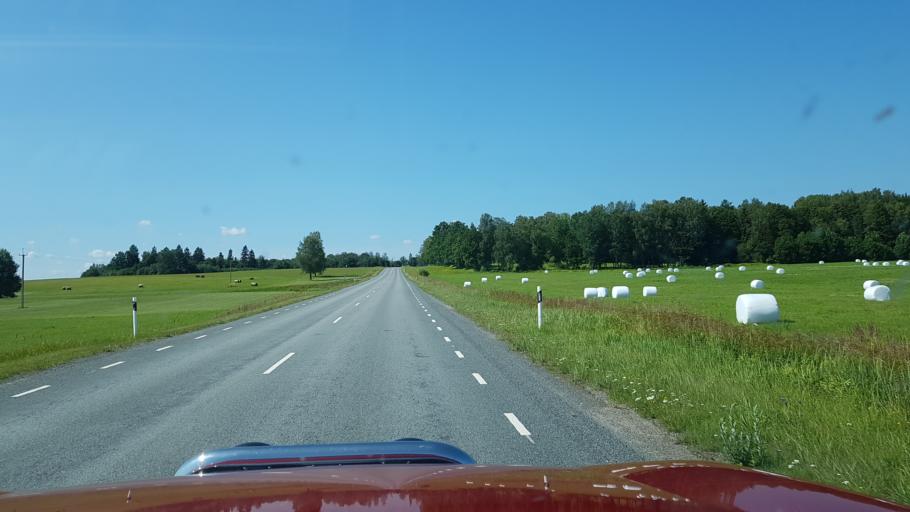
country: EE
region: Vorumaa
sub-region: Antsla vald
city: Vana-Antsla
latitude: 57.9526
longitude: 26.4407
